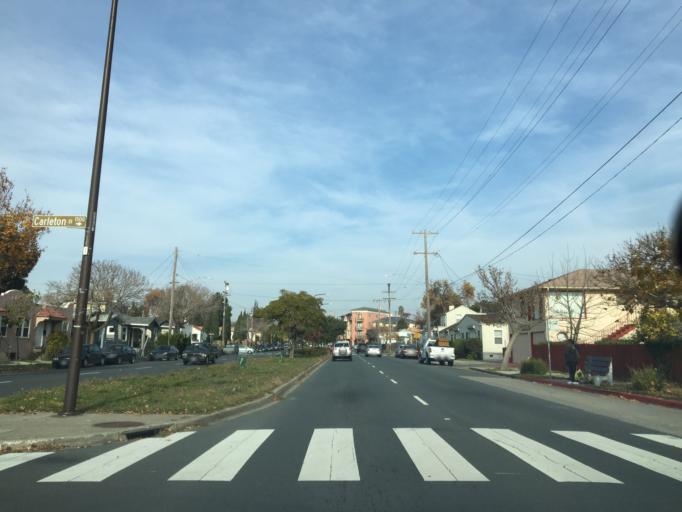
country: US
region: California
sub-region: Alameda County
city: Berkeley
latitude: 37.8595
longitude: -122.2803
